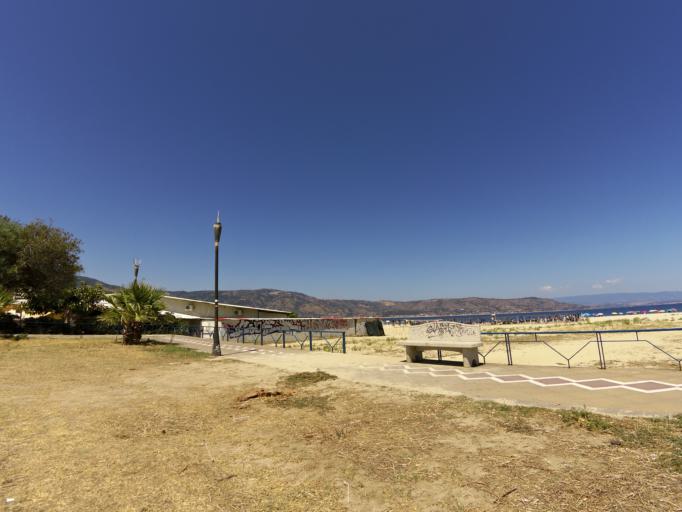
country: IT
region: Calabria
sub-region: Provincia di Catanzaro
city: Soverato Marina
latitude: 38.6903
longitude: 16.5531
